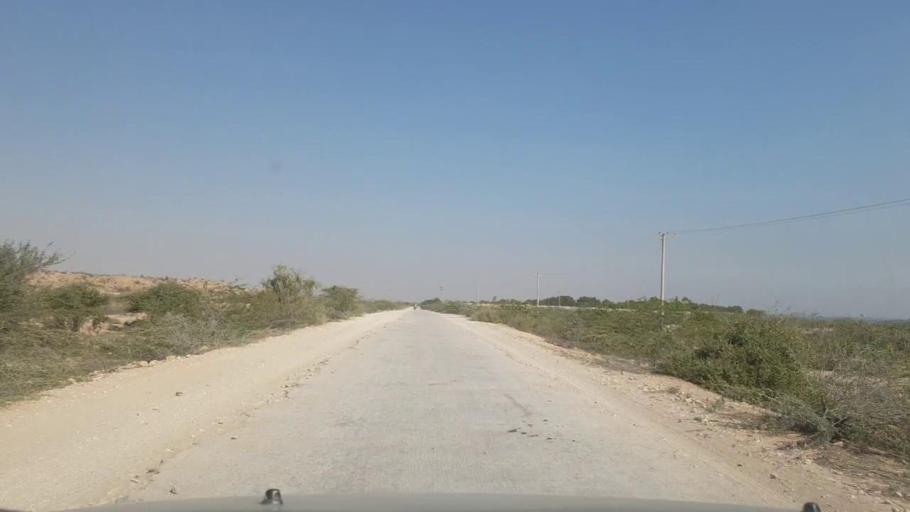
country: PK
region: Sindh
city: Thatta
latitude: 24.9877
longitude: 67.9999
